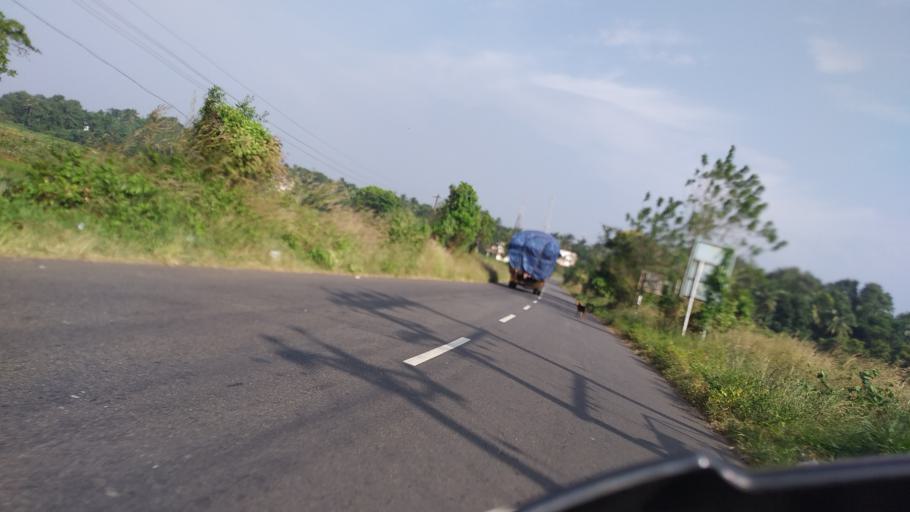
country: IN
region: Kerala
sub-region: Palakkad district
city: Palakkad
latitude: 10.6015
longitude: 76.5478
